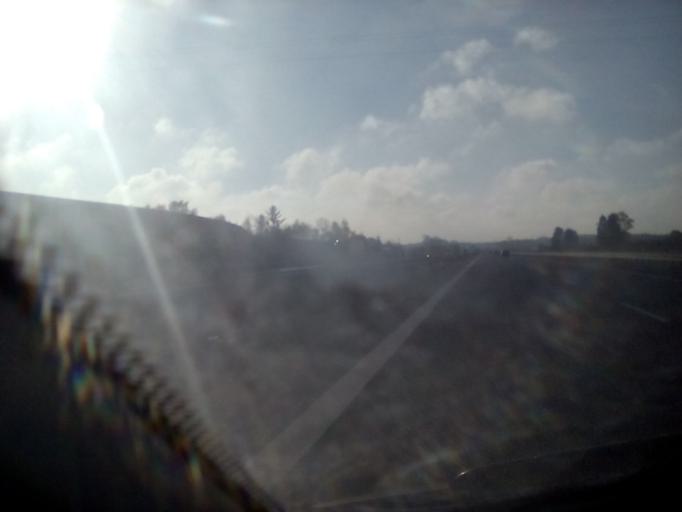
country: PL
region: Masovian Voivodeship
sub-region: Powiat grojecki
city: Grojec
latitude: 51.8118
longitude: 20.8851
